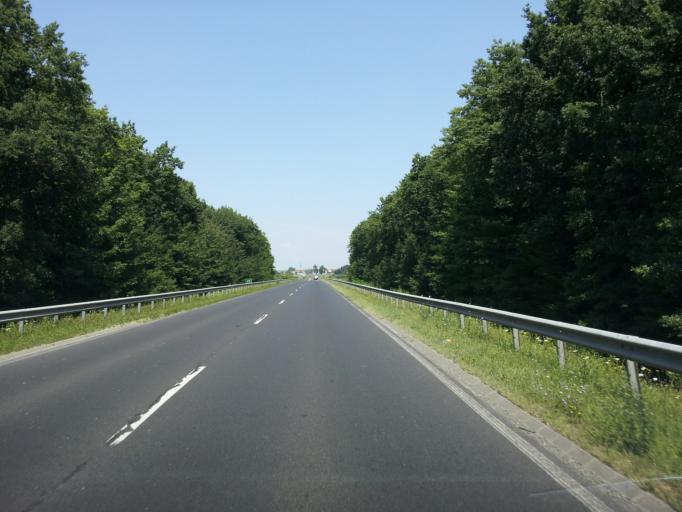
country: HU
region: Zala
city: Zalaegerszeg
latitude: 46.8499
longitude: 16.8629
